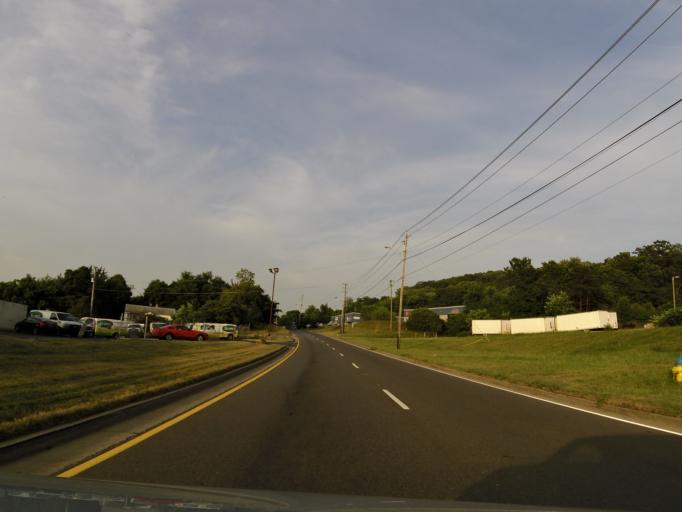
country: US
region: Tennessee
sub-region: Knox County
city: Knoxville
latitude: 35.9566
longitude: -84.0014
